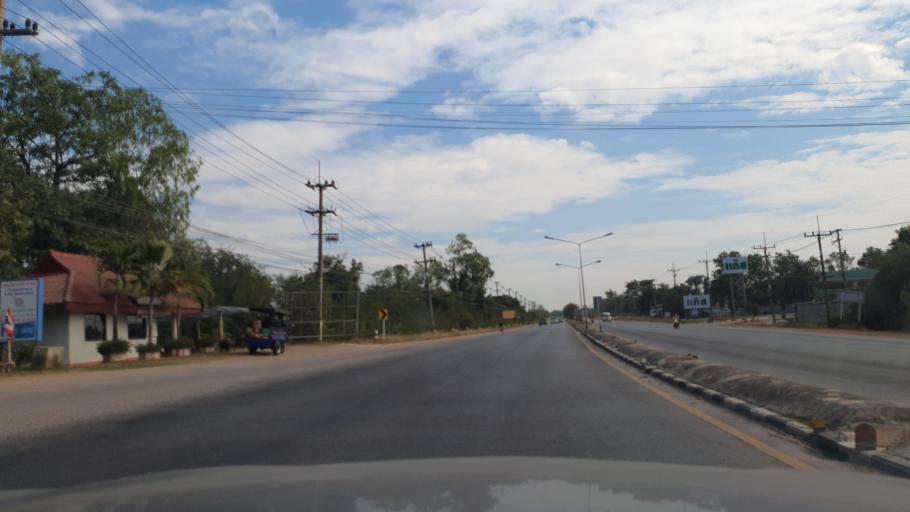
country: TH
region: Kalasin
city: Kalasin
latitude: 16.4102
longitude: 103.4547
